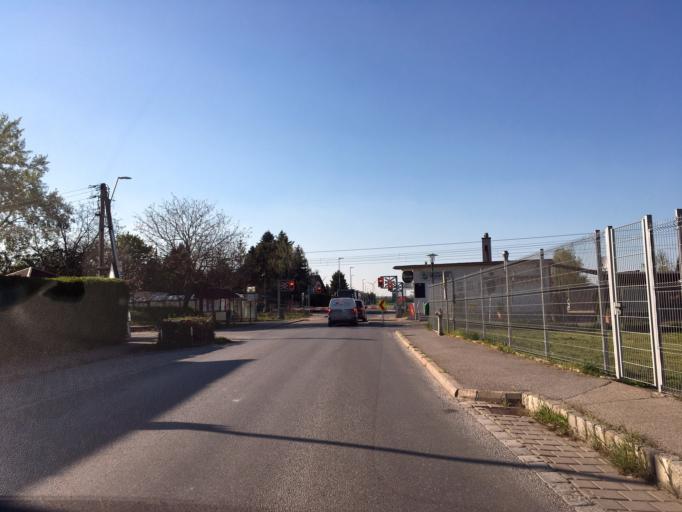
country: AT
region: Lower Austria
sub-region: Politischer Bezirk Ganserndorf
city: Strasshof an der Nordbahn
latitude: 48.3279
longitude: 16.6788
